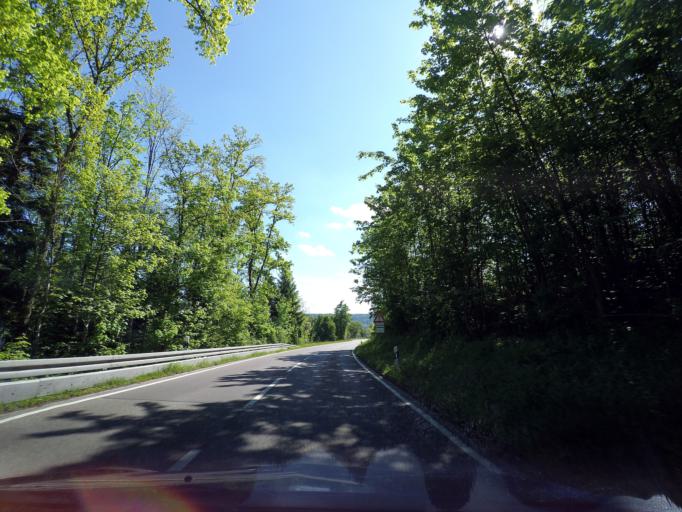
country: DE
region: Baden-Wuerttemberg
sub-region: Regierungsbezirk Stuttgart
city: Gaildorf
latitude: 48.9753
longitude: 9.7661
